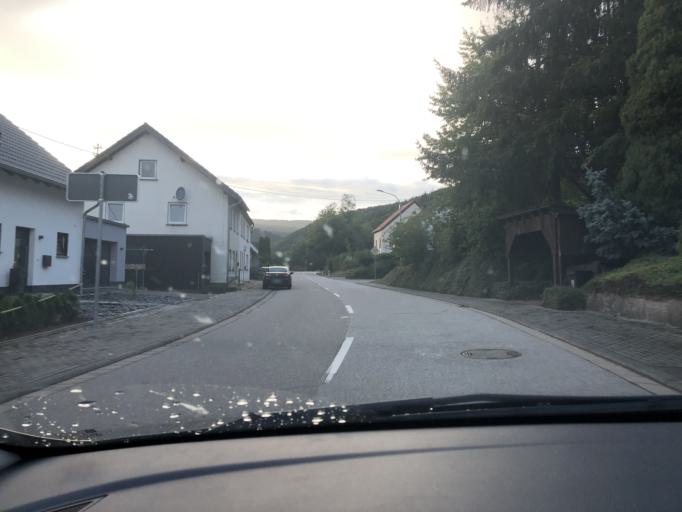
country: DE
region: Rheinland-Pfalz
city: Grimburg
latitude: 49.5855
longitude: 6.8869
